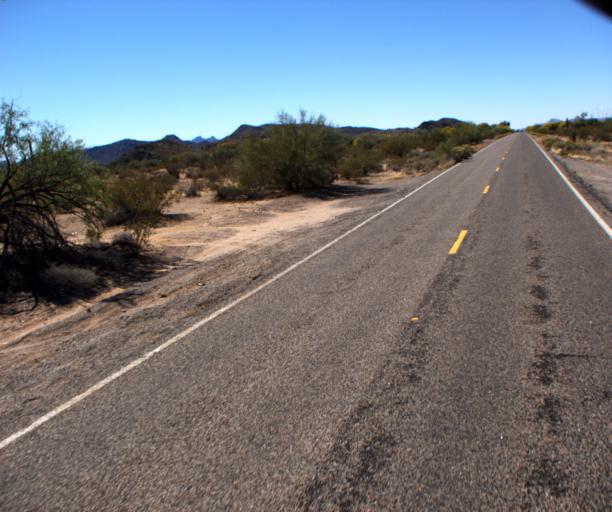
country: US
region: Arizona
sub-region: Pima County
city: Ajo
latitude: 32.2438
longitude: -112.7483
